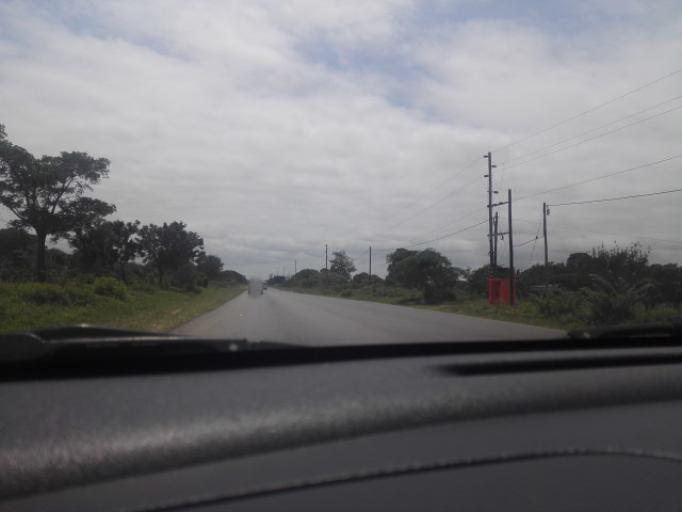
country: MZ
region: Maputo
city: Manhica
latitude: -25.4107
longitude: 32.7505
